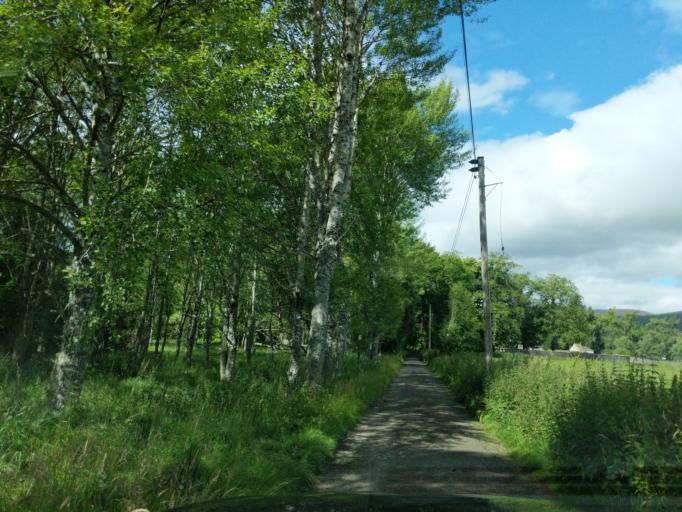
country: GB
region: Scotland
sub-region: Aberdeenshire
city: Ballater
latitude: 57.0370
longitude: -3.2108
